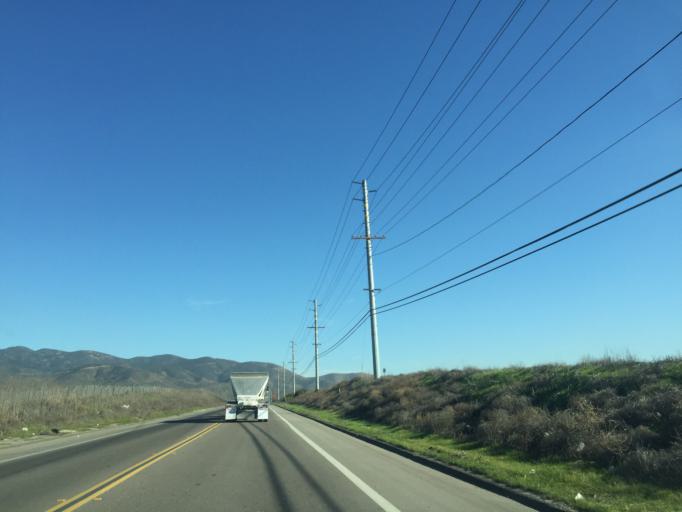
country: MX
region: Baja California
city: Tijuana
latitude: 32.5674
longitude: -116.9327
